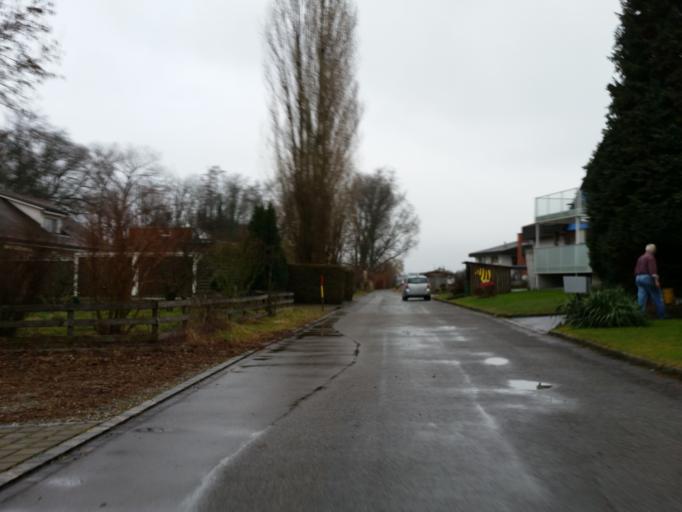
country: CH
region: Thurgau
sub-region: Arbon District
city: Egnach
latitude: 47.5437
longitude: 9.3875
